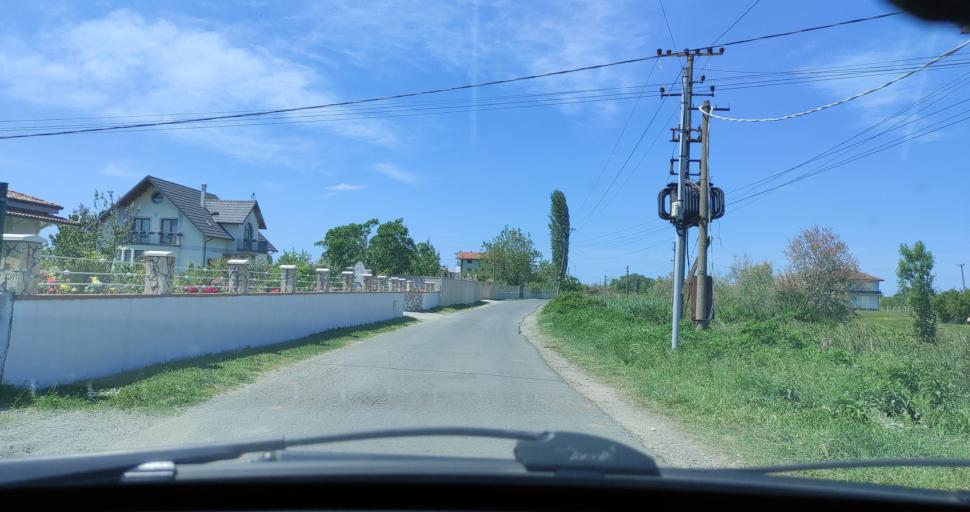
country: AL
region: Lezhe
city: Lezhe
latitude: 41.7564
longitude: 19.6161
